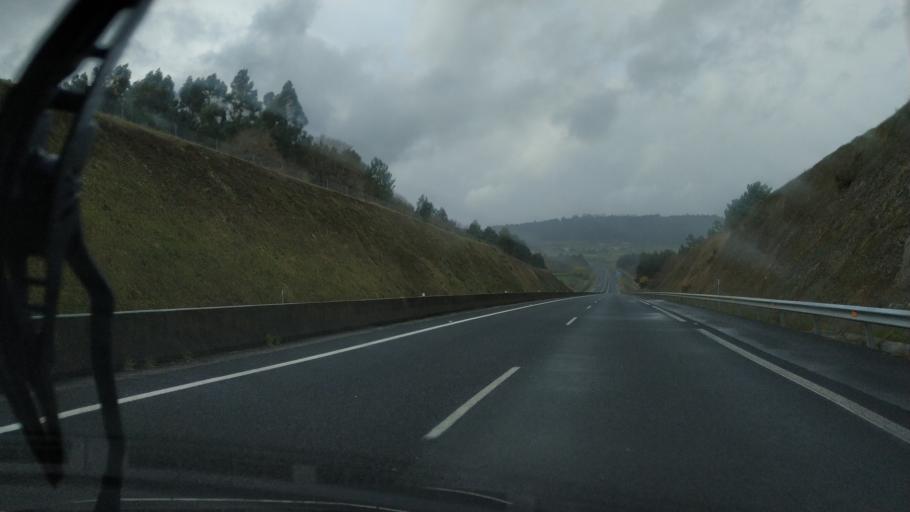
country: ES
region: Galicia
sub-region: Provincia de Pontevedra
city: Silleda
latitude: 42.7221
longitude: -8.3137
